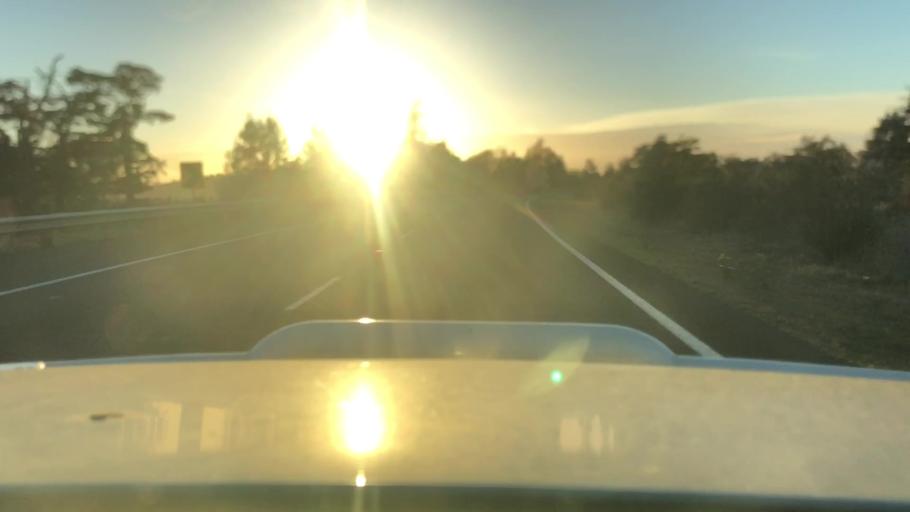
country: AU
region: New South Wales
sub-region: Goulburn Mulwaree
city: Goulburn
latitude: -34.7868
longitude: 149.6284
